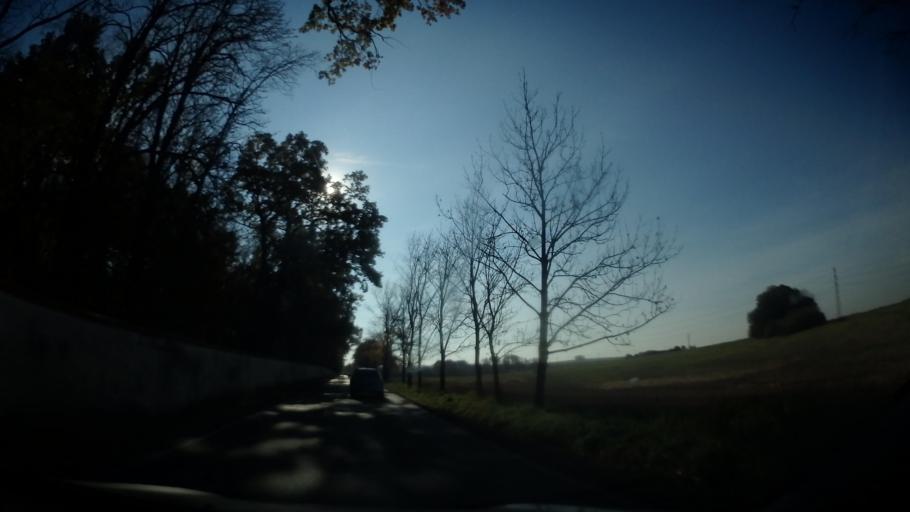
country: CZ
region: Praha
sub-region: Praha 20
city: Horni Pocernice
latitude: 50.0604
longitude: 14.6273
